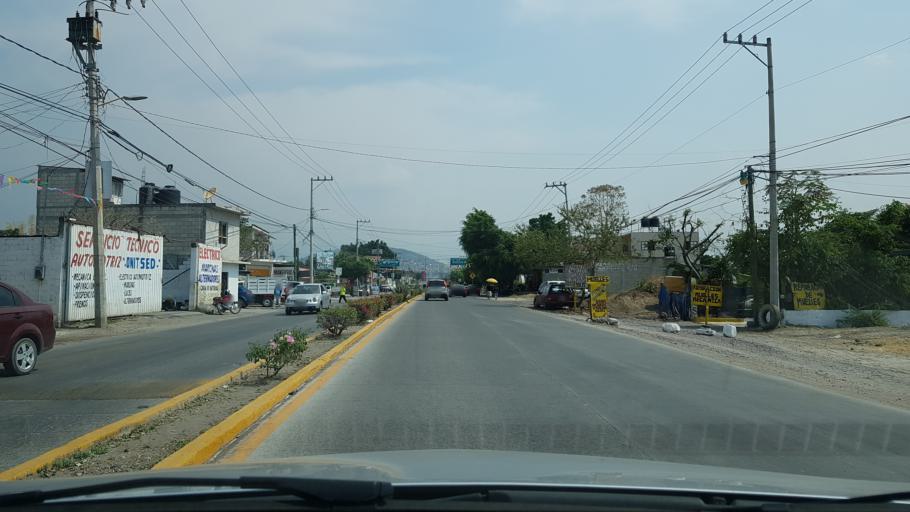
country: MX
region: Morelos
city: Emiliano Zapata
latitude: 18.8172
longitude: -99.1914
